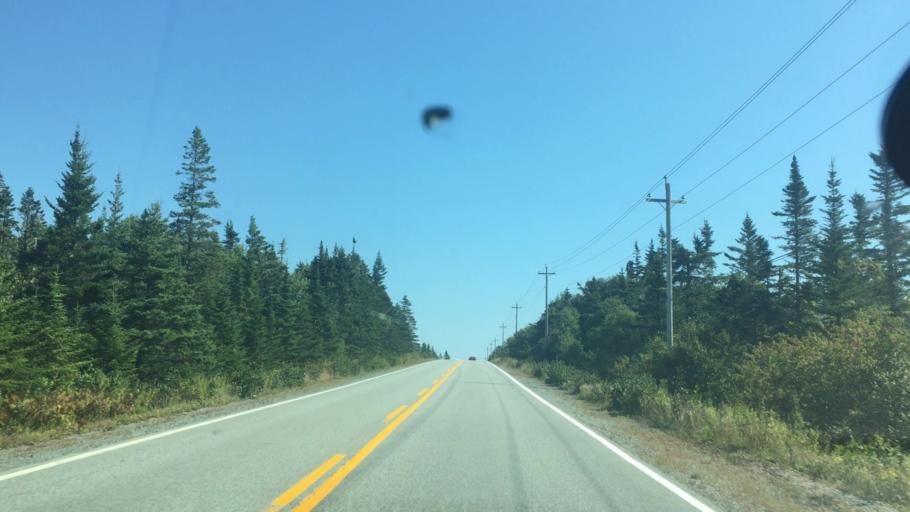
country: CA
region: Nova Scotia
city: Antigonish
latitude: 44.9326
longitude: -62.2875
